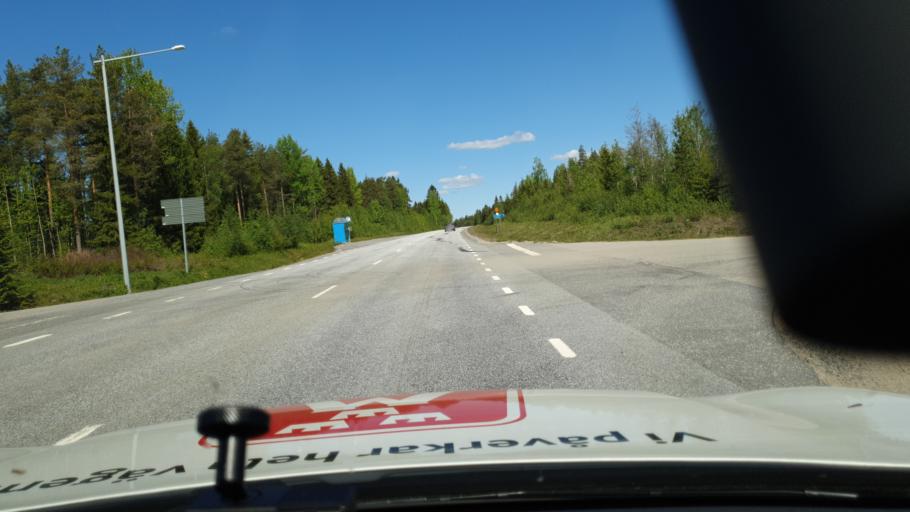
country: SE
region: Vaesterbotten
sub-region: Vannas Kommun
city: Vaennaes
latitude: 63.9976
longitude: 19.7259
